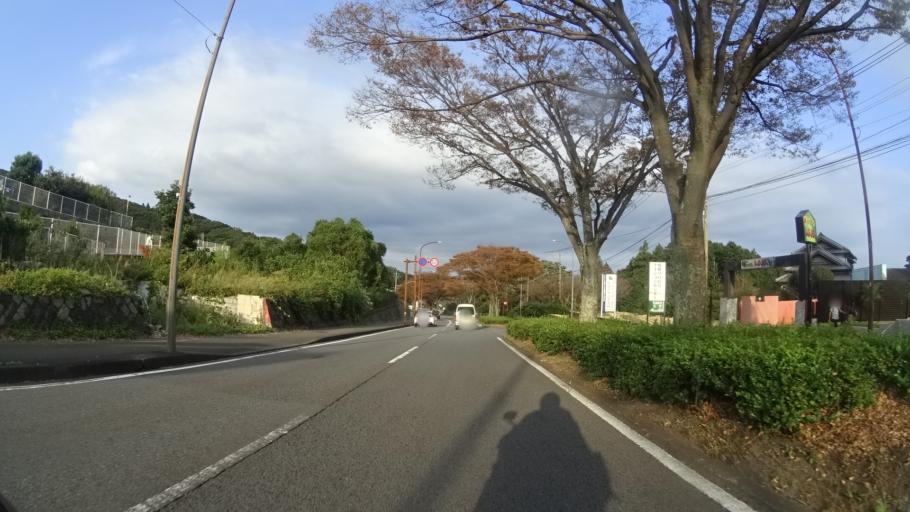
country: JP
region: Oita
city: Beppu
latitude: 33.3134
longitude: 131.4689
